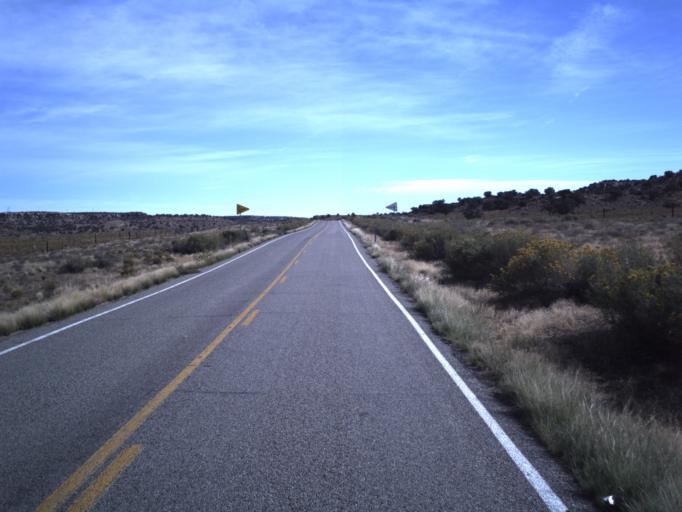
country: US
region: Utah
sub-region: San Juan County
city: Blanding
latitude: 37.4312
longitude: -109.4055
